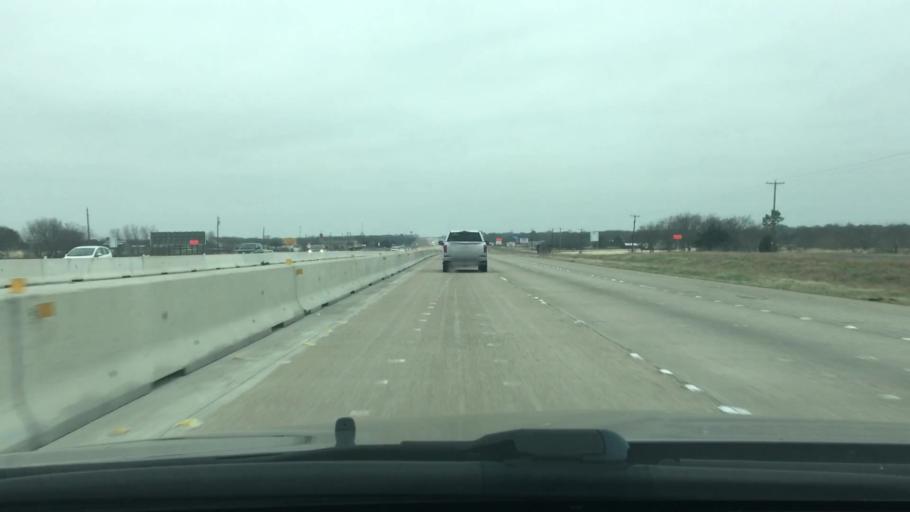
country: US
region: Texas
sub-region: Navarro County
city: Corsicana
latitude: 32.0304
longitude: -96.4429
